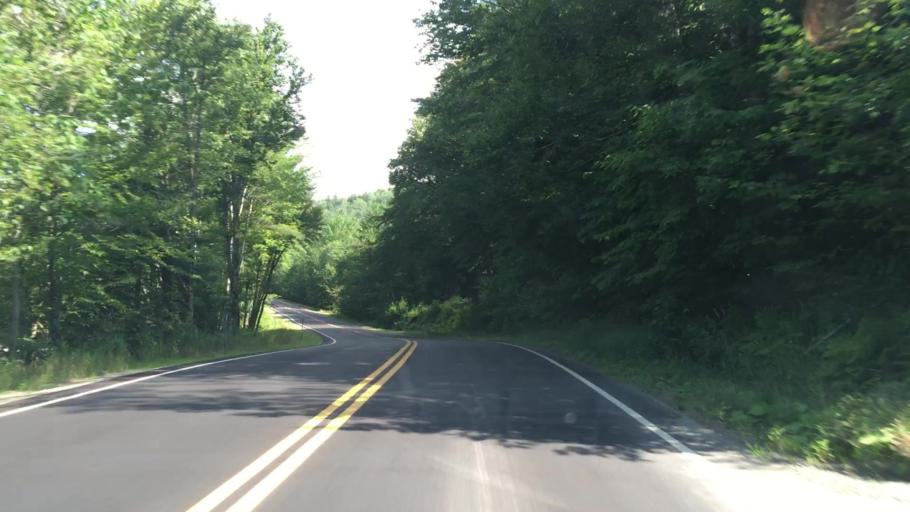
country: US
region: New Hampshire
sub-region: Grafton County
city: North Haverhill
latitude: 44.1116
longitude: -71.9036
